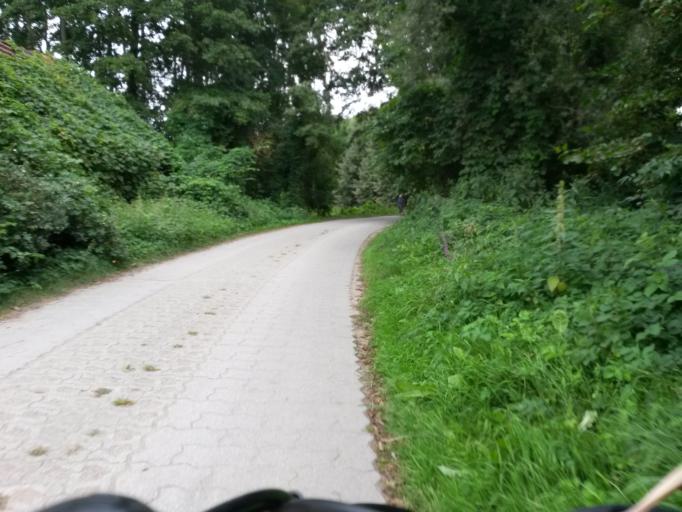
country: DE
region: Brandenburg
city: Angermunde
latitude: 53.0369
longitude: 13.9447
